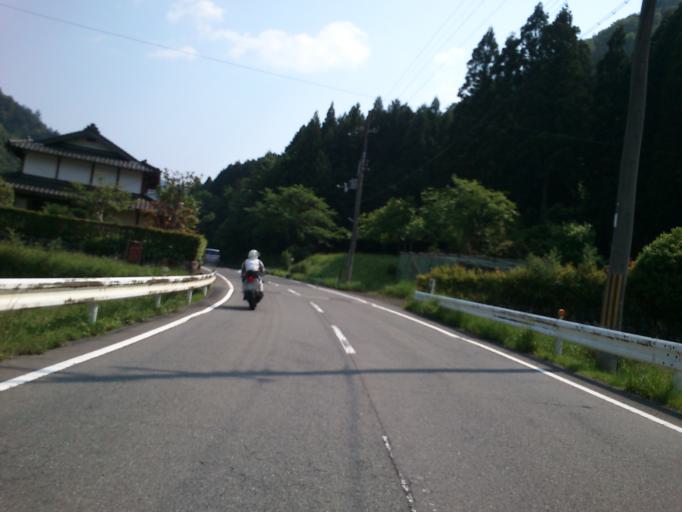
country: JP
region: Kyoto
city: Kameoka
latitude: 35.2523
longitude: 135.5619
